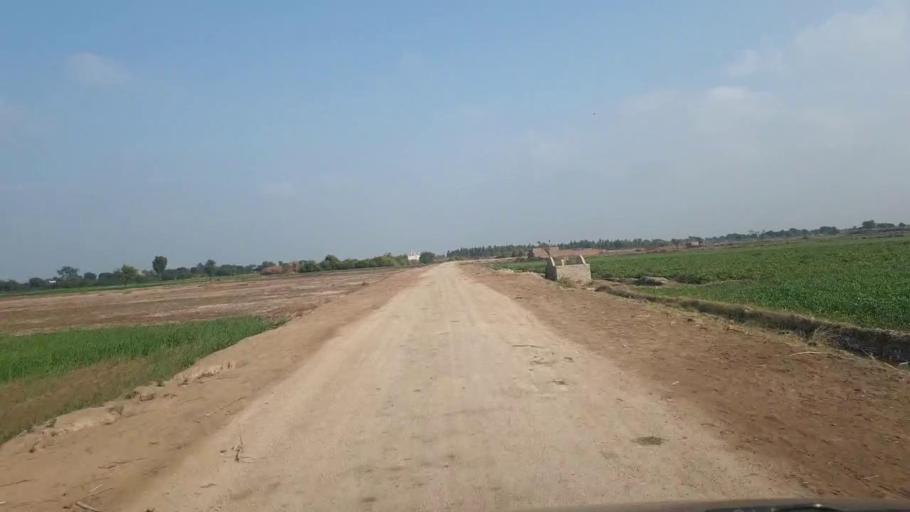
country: PK
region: Sindh
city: Shahdadpur
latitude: 25.9132
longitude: 68.6794
